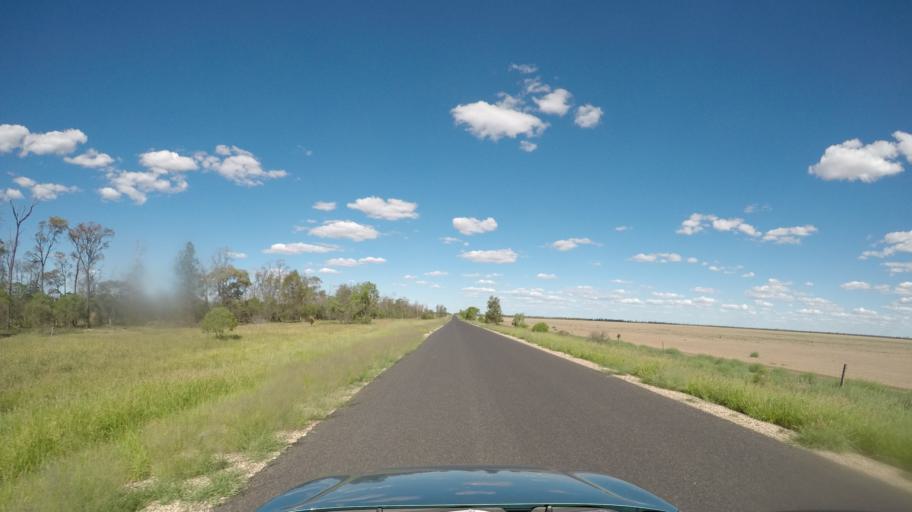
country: AU
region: Queensland
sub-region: Goondiwindi
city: Goondiwindi
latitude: -28.1632
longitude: 150.1549
